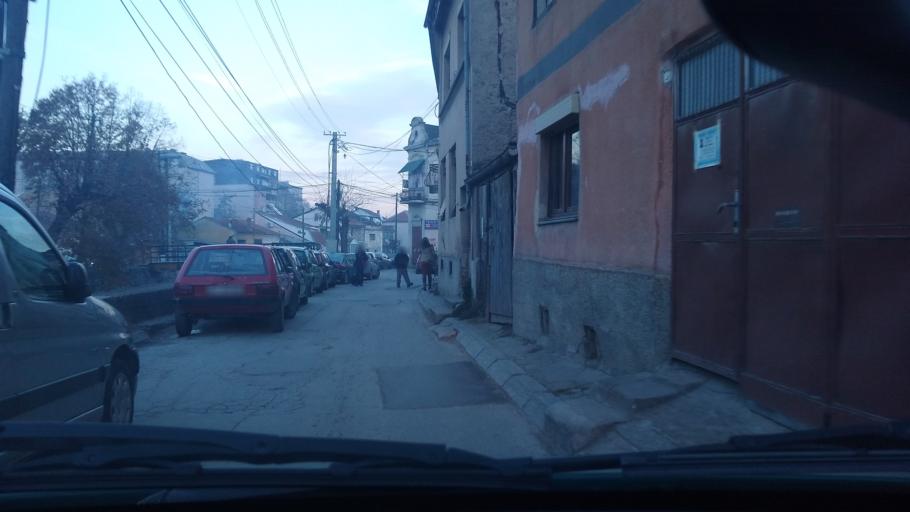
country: MK
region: Bitola
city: Bitola
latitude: 41.0315
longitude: 21.3393
